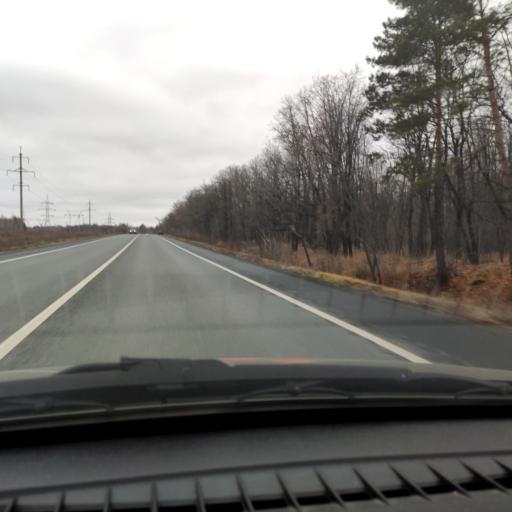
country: RU
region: Samara
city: Bogatyr'
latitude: 53.5067
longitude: 49.9380
